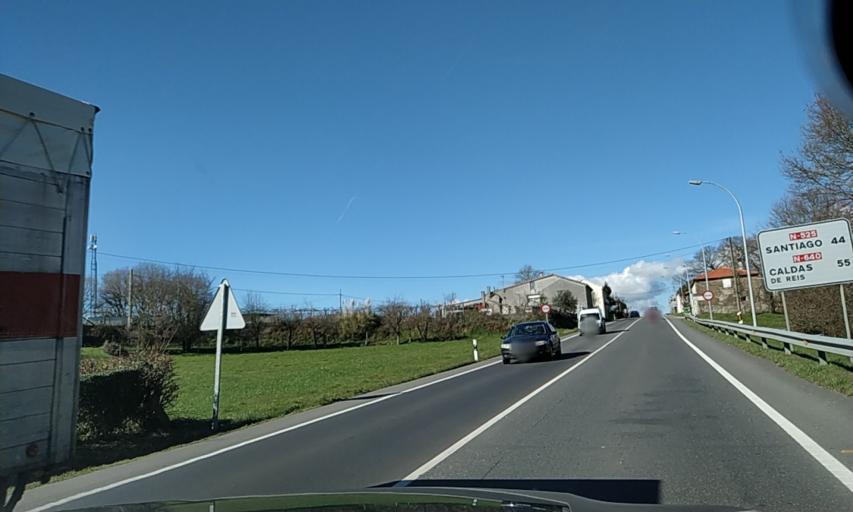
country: ES
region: Galicia
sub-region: Provincia de Pontevedra
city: Lalin
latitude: 42.6763
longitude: -8.1648
